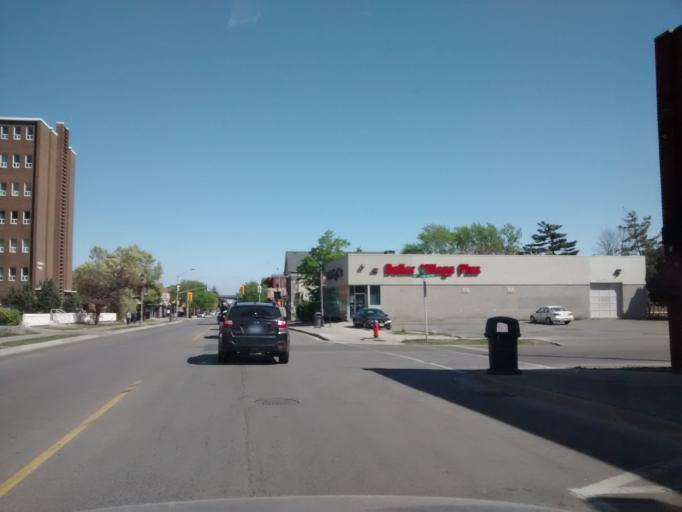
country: CA
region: Ontario
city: Oakville
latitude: 43.4454
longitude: -79.6846
